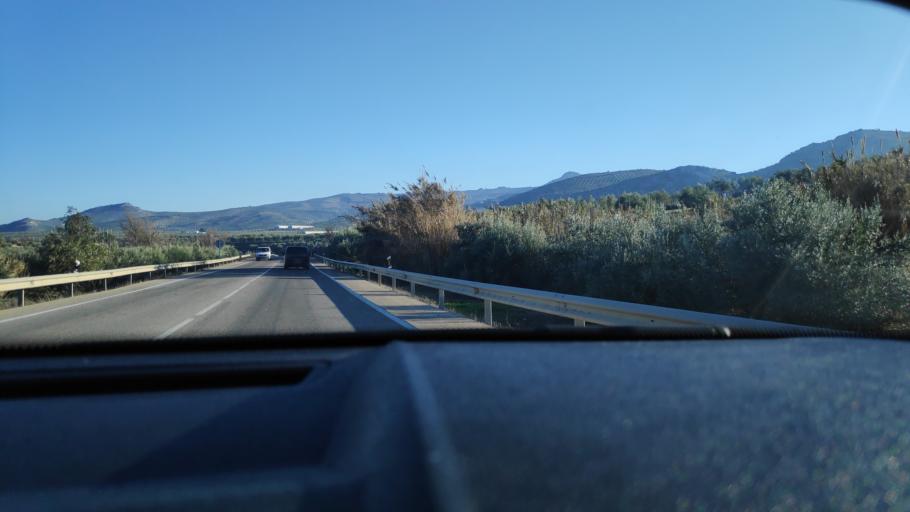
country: ES
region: Andalusia
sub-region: Province of Cordoba
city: Luque
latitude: 37.5698
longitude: -4.2509
